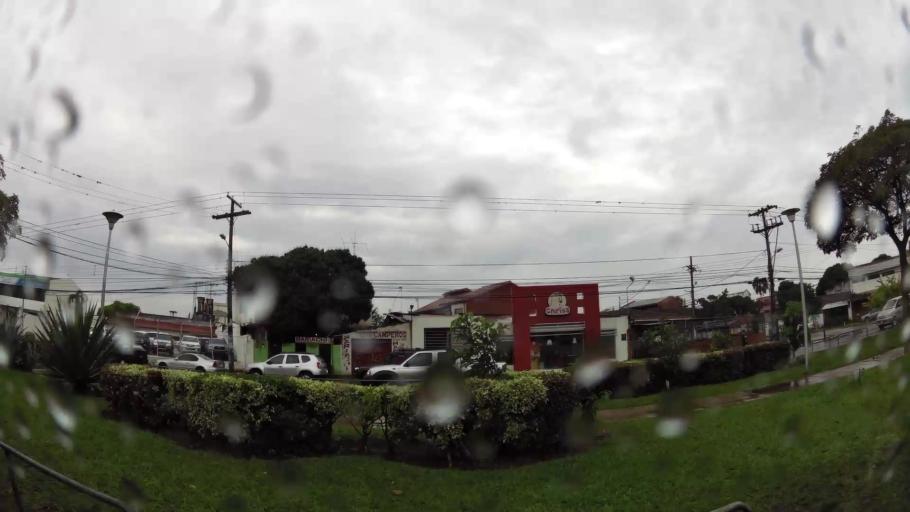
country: BO
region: Santa Cruz
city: Santa Cruz de la Sierra
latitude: -17.7905
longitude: -63.1721
